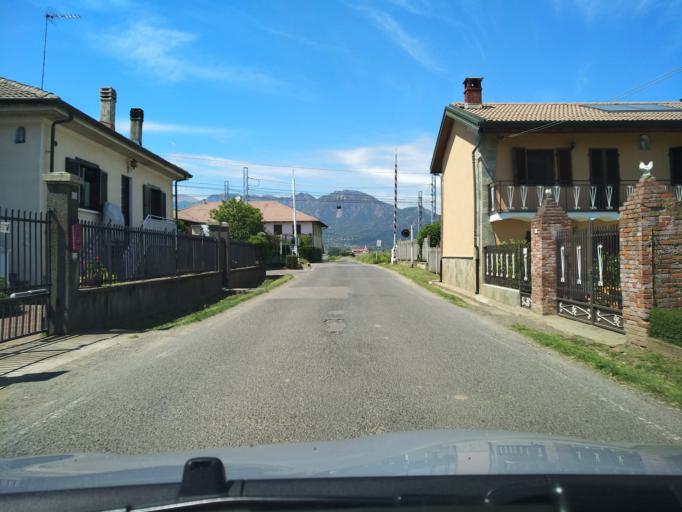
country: IT
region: Piedmont
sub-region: Provincia di Torino
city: Riva
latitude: 44.9039
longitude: 7.3778
